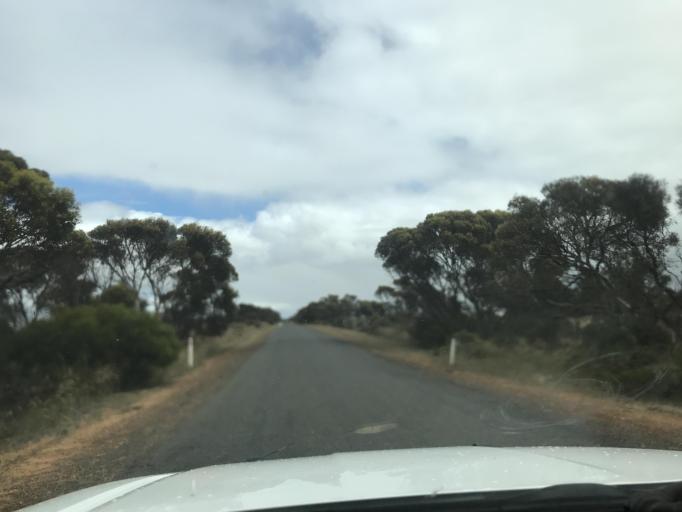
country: AU
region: South Australia
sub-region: Tatiara
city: Bordertown
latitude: -36.1448
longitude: 141.2315
